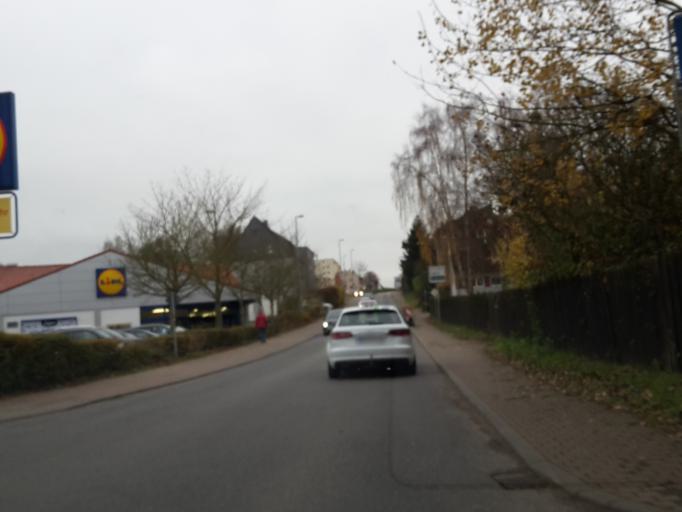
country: DE
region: Hesse
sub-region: Regierungsbezirk Darmstadt
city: Idstein
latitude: 50.2293
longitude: 8.2638
